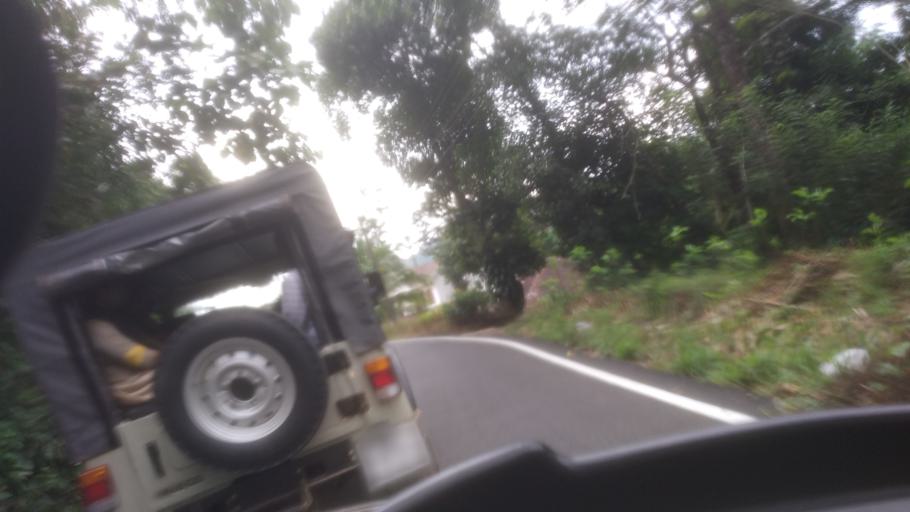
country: IN
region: Kerala
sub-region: Idukki
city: Idukki
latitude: 9.9407
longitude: 77.0265
